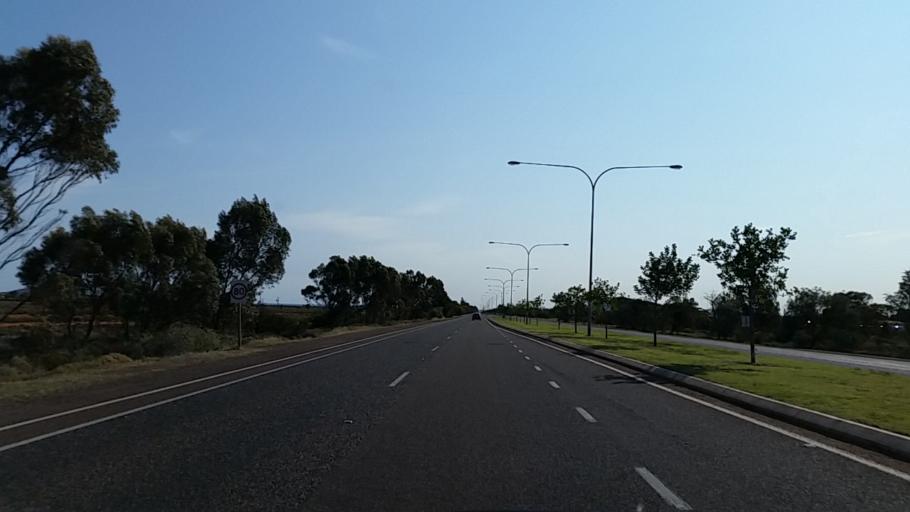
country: AU
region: South Australia
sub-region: Whyalla
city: Whyalla
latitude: -33.0406
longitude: 137.5520
